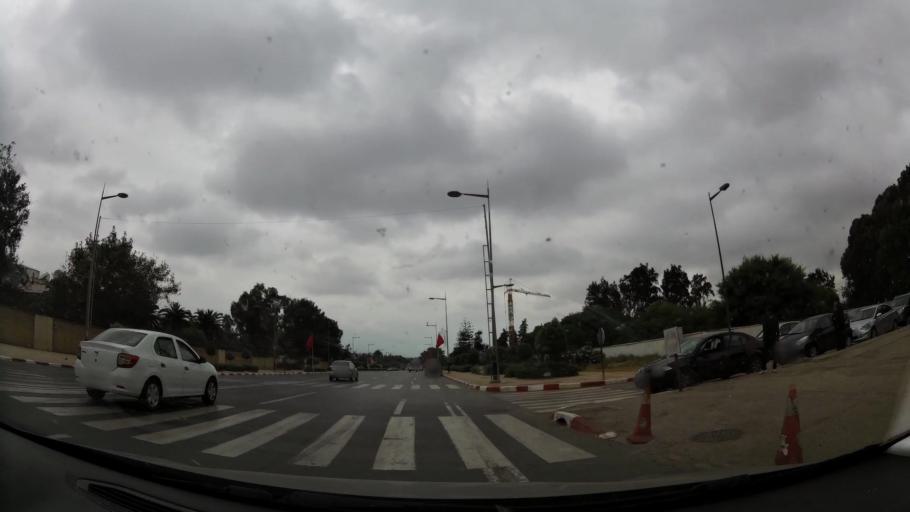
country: MA
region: Rabat-Sale-Zemmour-Zaer
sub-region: Rabat
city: Rabat
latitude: 33.9691
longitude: -6.8286
